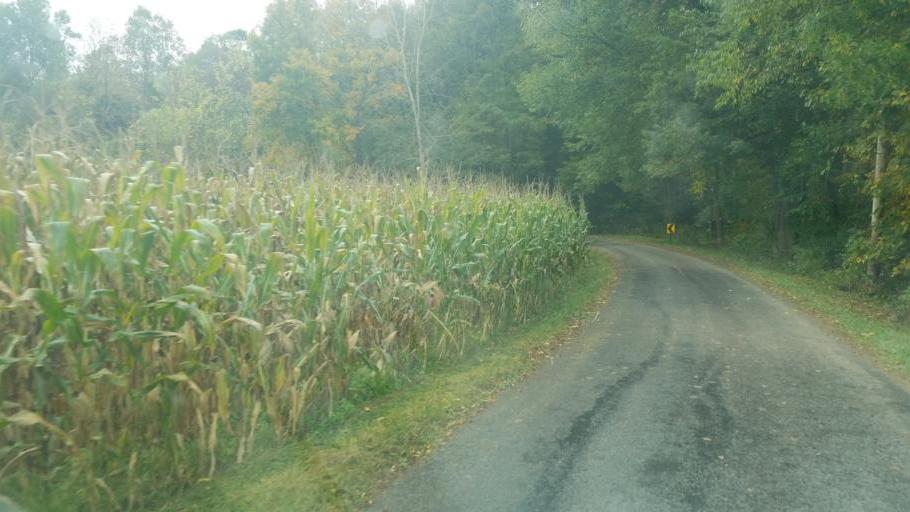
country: US
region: Ohio
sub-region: Holmes County
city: Millersburg
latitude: 40.5802
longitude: -81.8684
